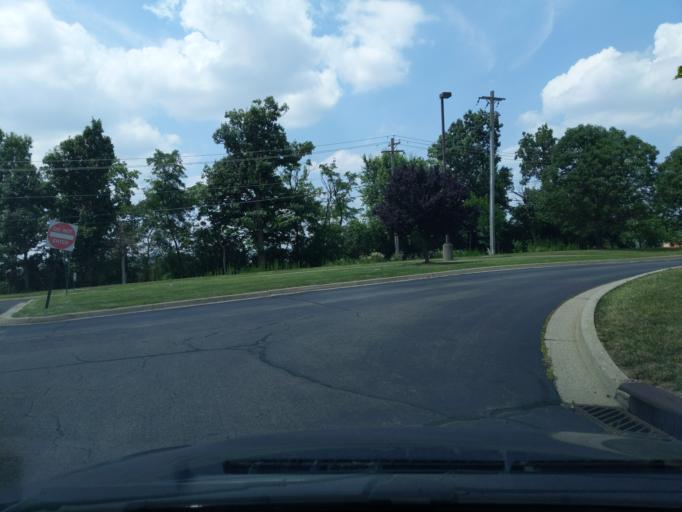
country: US
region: Ohio
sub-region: Hamilton County
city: Glendale
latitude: 39.2860
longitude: -84.4555
